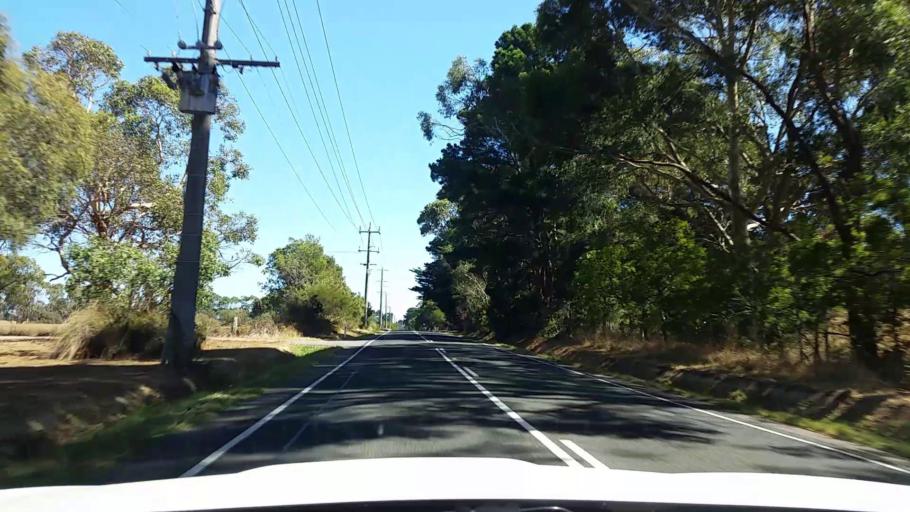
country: AU
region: Victoria
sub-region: Mornington Peninsula
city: Hastings
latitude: -38.2846
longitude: 145.1372
